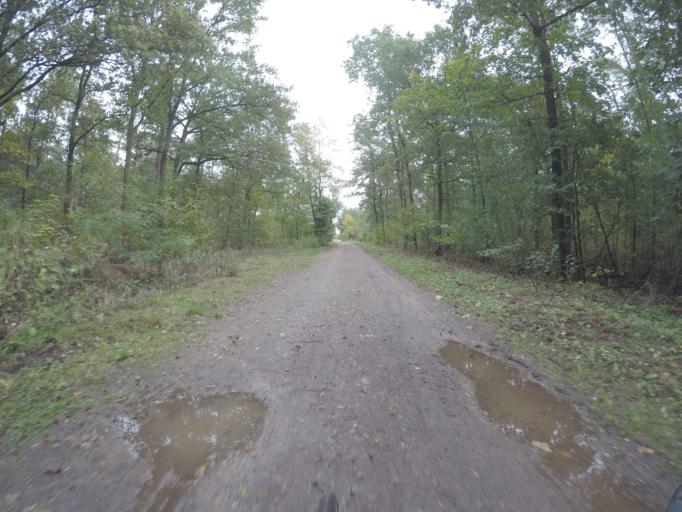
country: DE
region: Berlin
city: Buch
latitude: 52.6535
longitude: 13.4913
